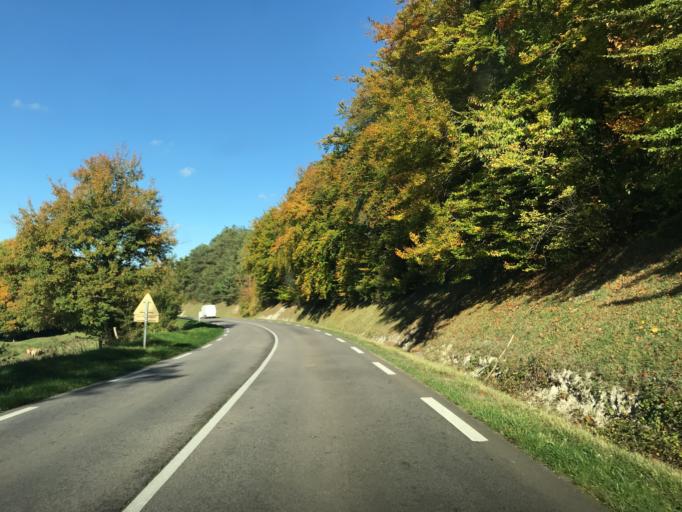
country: FR
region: Haute-Normandie
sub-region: Departement de l'Eure
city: Saint-Aubin-sur-Gaillon
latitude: 49.0812
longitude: 1.2627
